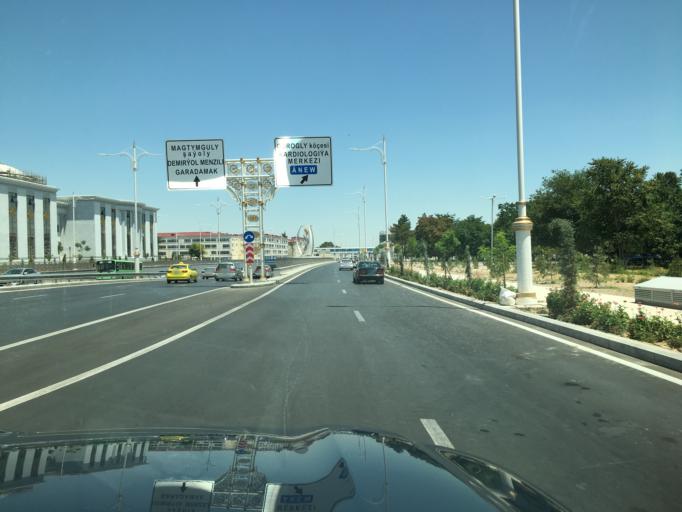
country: TM
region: Ahal
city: Ashgabat
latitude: 37.9311
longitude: 58.3935
